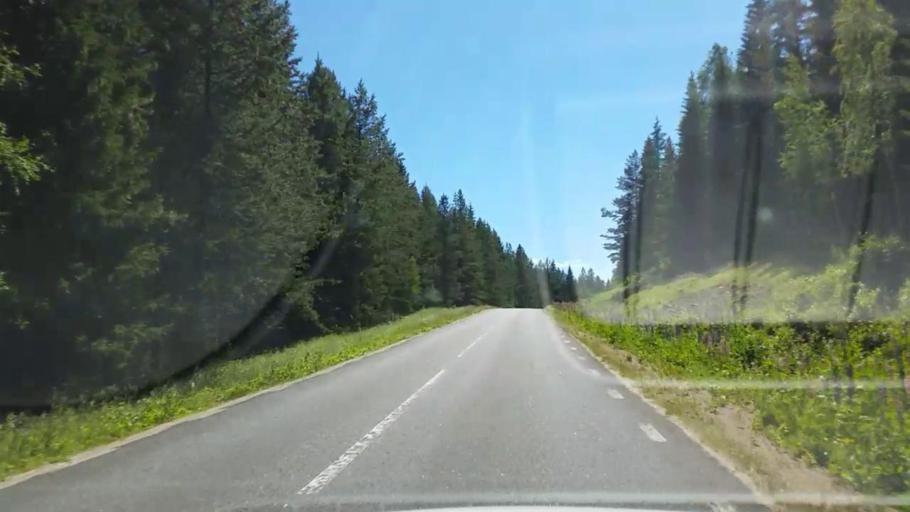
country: SE
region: Gaevleborg
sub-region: Ljusdals Kommun
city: Farila
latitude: 61.6617
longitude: 15.6042
